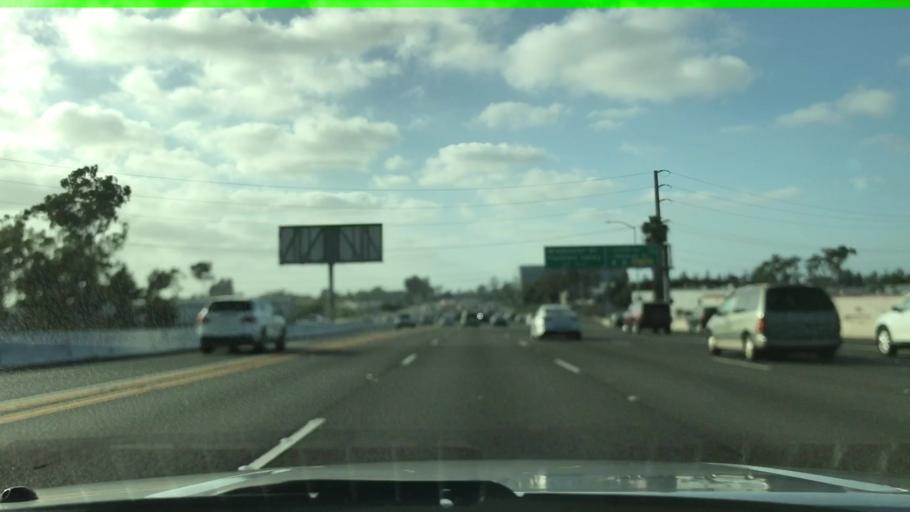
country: US
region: California
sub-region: Orange County
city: Fountain Valley
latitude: 33.6960
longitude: -117.9356
